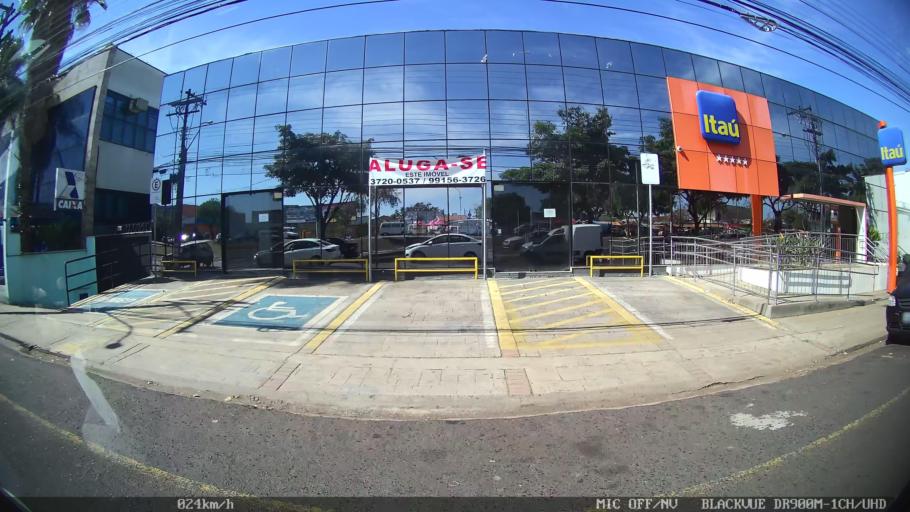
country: BR
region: Sao Paulo
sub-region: Franca
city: Franca
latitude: -20.5309
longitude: -47.4126
